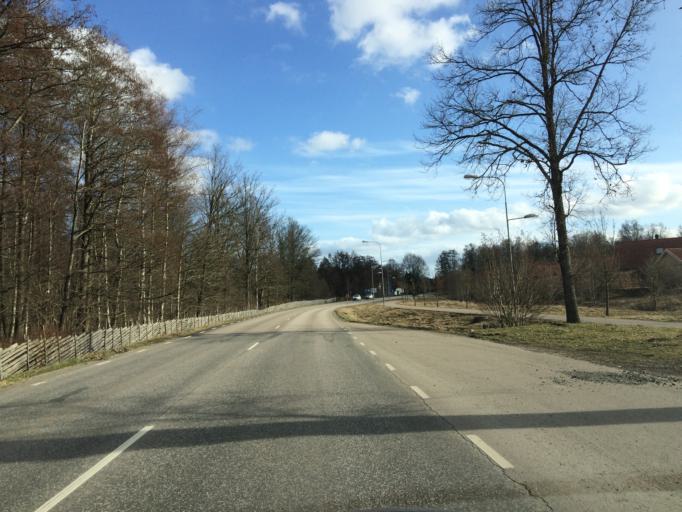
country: SE
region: Kronoberg
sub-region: Almhults Kommun
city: AElmhult
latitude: 56.5643
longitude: 14.1289
